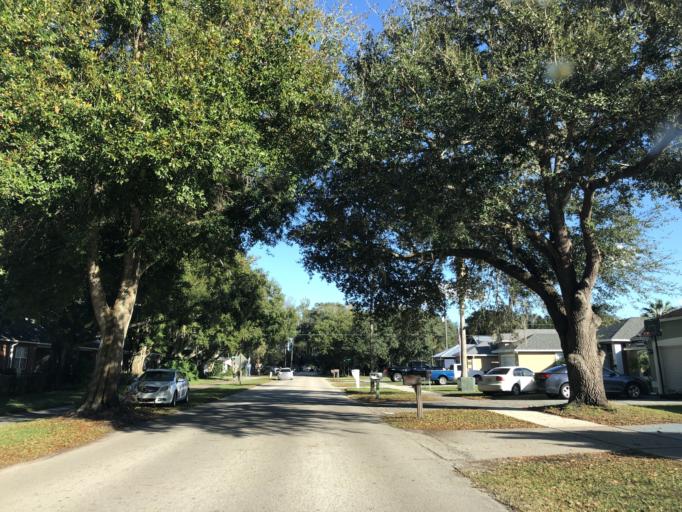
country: US
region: Florida
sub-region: Osceola County
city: Saint Cloud
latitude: 28.2533
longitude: -81.3086
